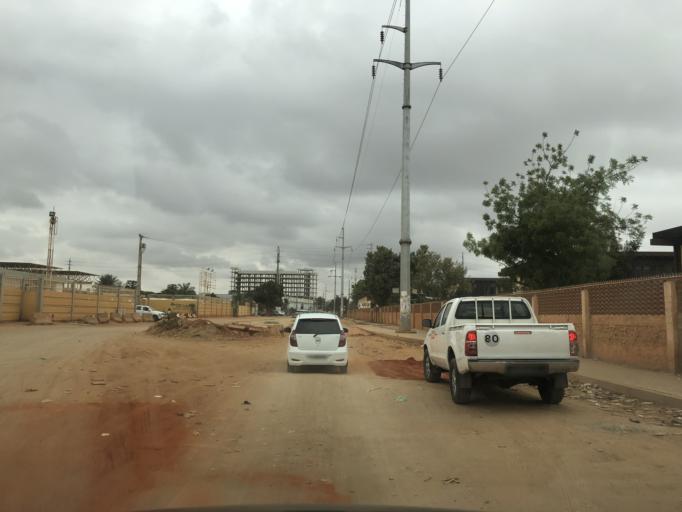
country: AO
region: Luanda
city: Luanda
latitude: -8.9000
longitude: 13.1975
